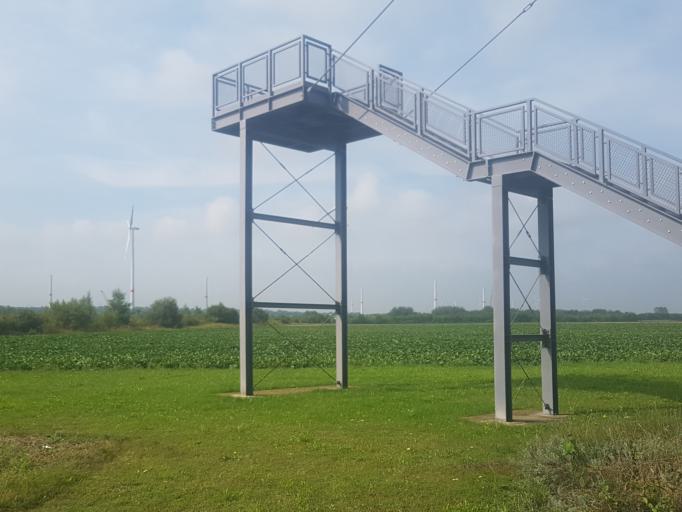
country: DE
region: North Rhine-Westphalia
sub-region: Regierungsbezirk Koln
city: Aldenhoven
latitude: 50.8876
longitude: 6.3143
